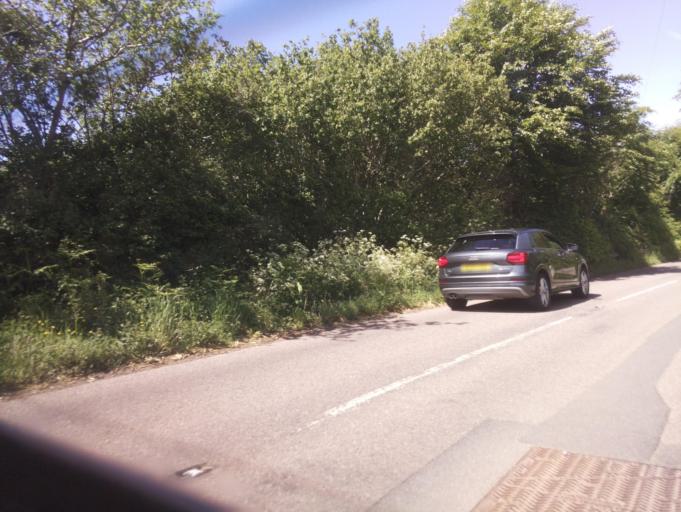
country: GB
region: England
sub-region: Devon
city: Newton Poppleford
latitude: 50.7060
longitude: -3.2678
